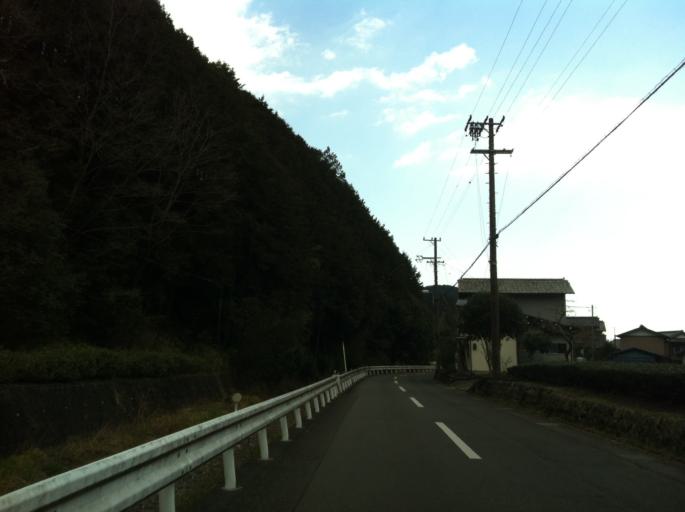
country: JP
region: Shizuoka
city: Shizuoka-shi
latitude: 35.0311
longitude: 138.3376
